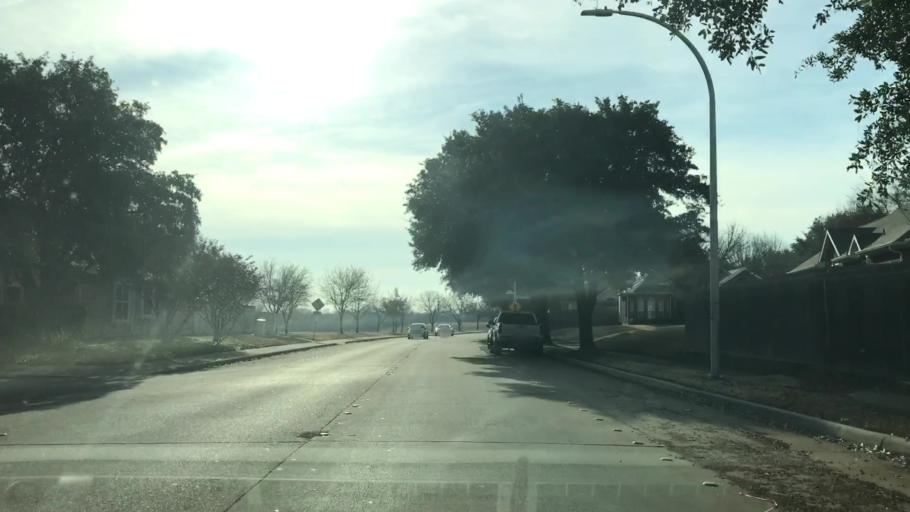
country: US
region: Texas
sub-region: Tarrant County
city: Watauga
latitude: 32.8748
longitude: -97.2793
